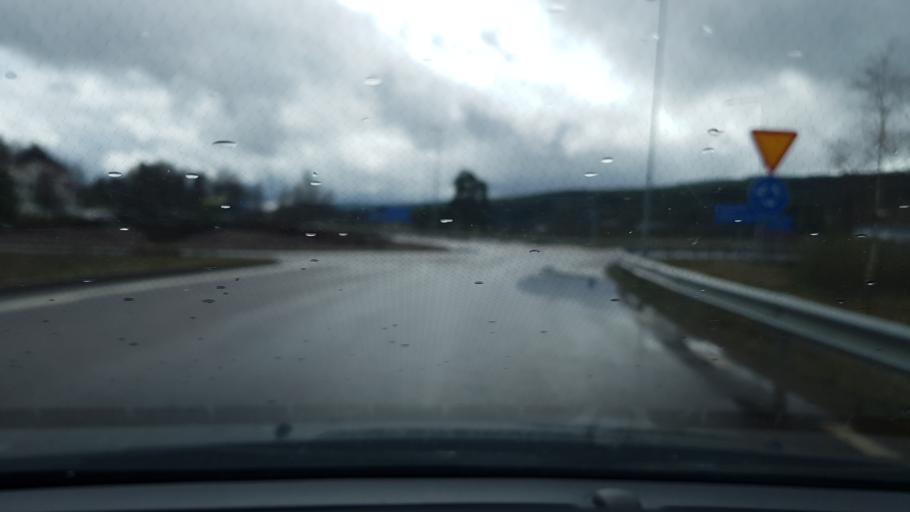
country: SE
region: Dalarna
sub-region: Malung-Saelens kommun
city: Malung
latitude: 61.1497
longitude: 13.2725
